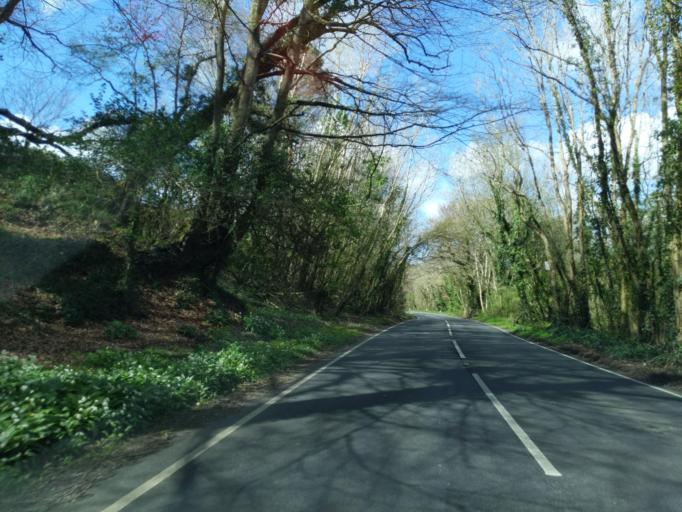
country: GB
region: England
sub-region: Cornwall
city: Helland
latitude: 50.5017
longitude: -4.7762
